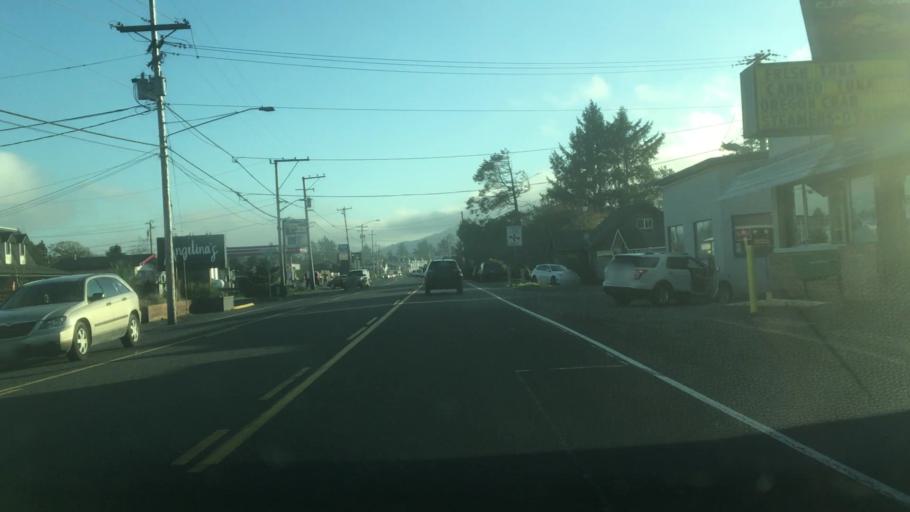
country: US
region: Oregon
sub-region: Clatsop County
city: Seaside
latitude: 45.9825
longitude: -123.9261
